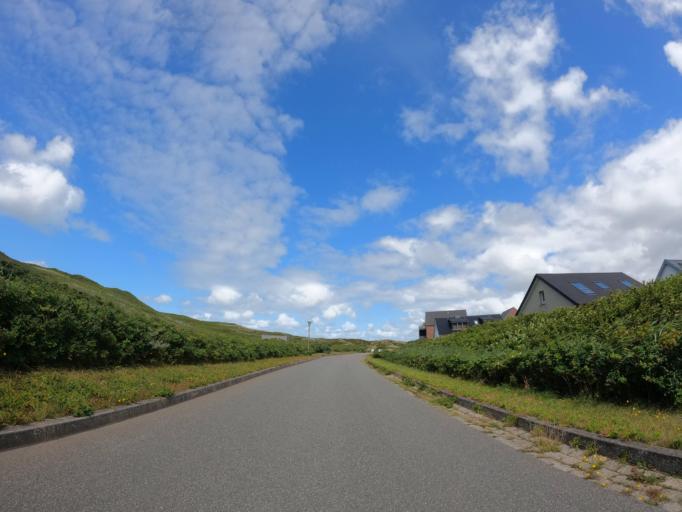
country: DE
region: Schleswig-Holstein
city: Westerland
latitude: 54.8558
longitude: 8.2893
